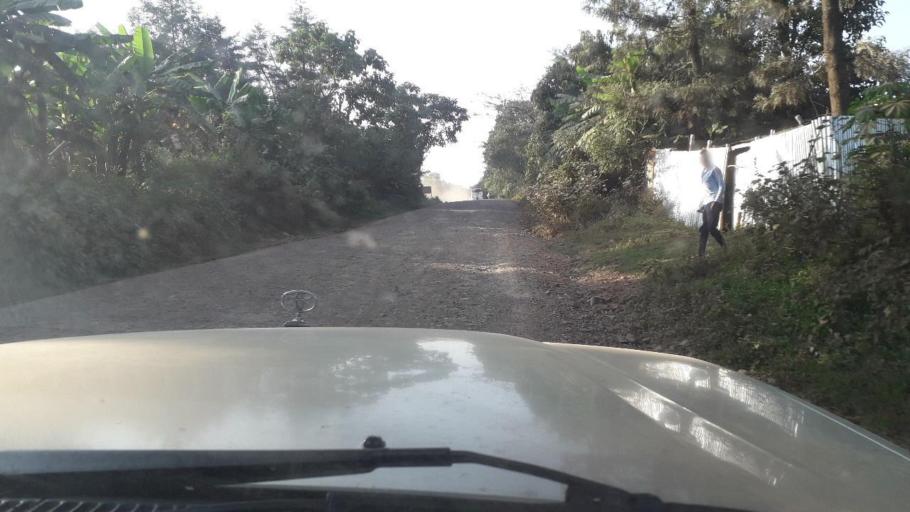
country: ET
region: Oromiya
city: Jima
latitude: 7.5973
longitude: 36.8468
